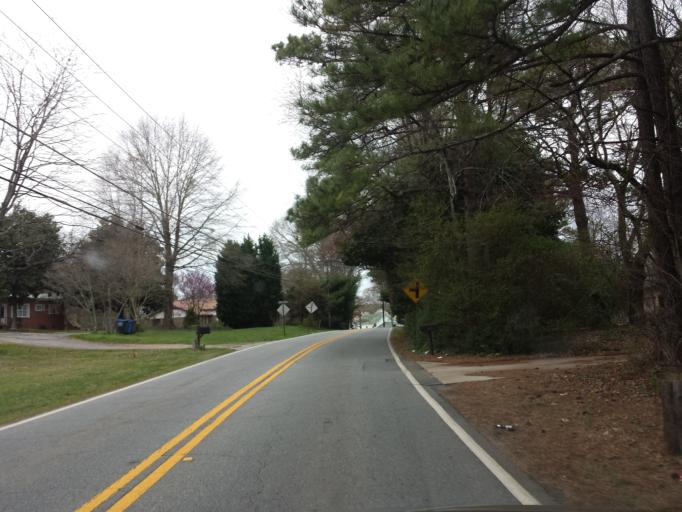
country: US
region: Georgia
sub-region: Cherokee County
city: Woodstock
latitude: 34.0373
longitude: -84.5075
